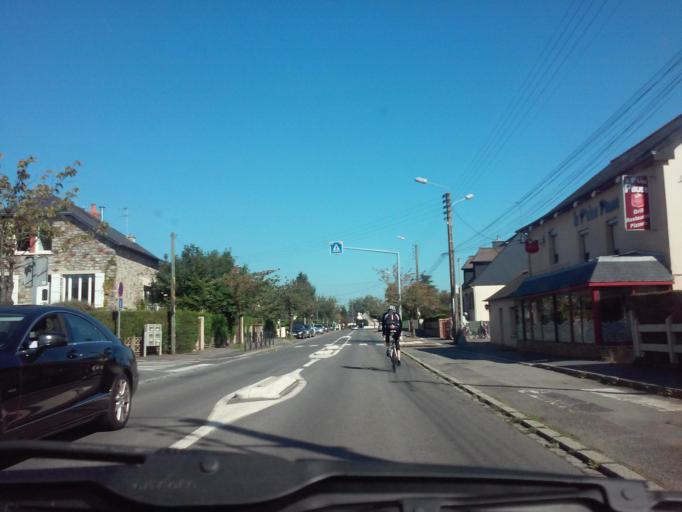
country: FR
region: Brittany
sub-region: Departement d'Ille-et-Vilaine
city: Betton
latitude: 48.1762
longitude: -1.6396
